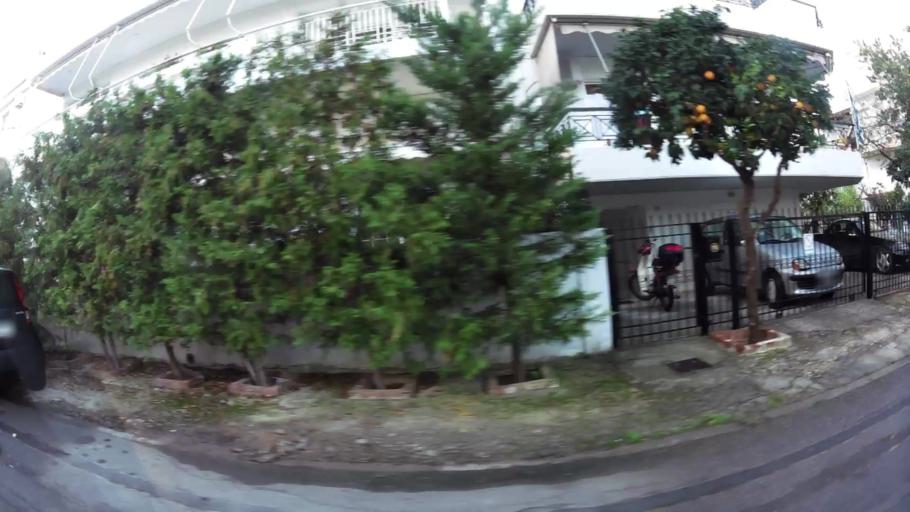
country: GR
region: Attica
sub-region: Nomarchia Athinas
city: Marousi
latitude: 38.0412
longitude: 23.8107
